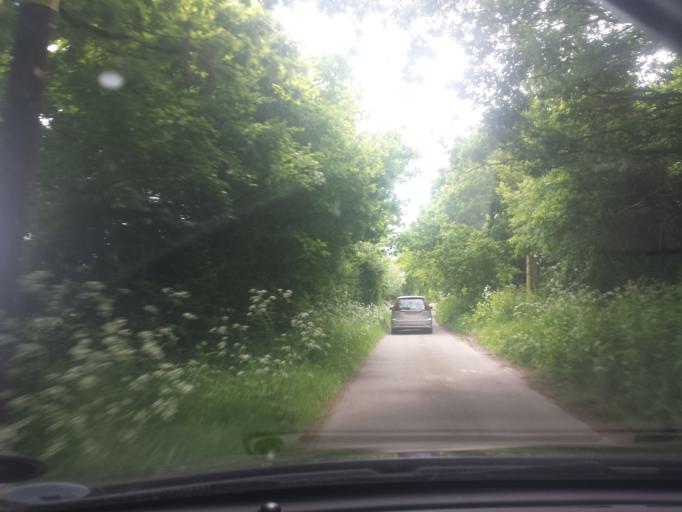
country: GB
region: England
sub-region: Essex
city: Little Clacton
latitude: 51.8669
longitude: 1.1384
